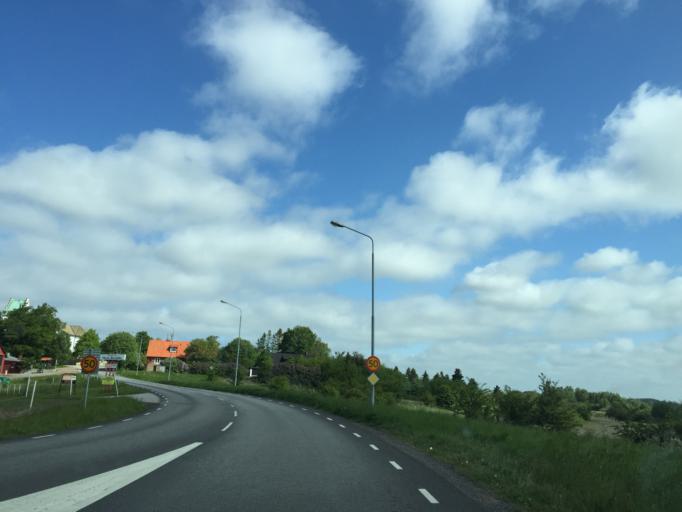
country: SE
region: Skane
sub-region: Malmo
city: Oxie
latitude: 55.5753
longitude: 13.0858
